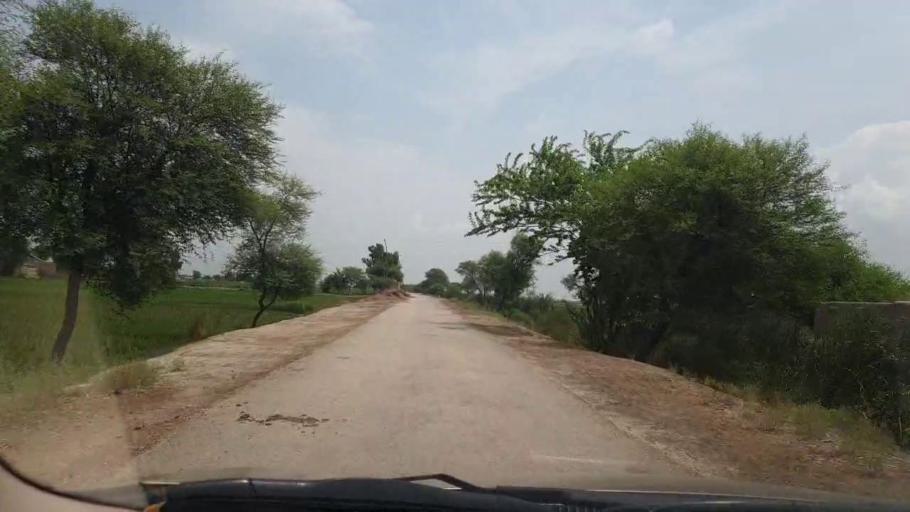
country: PK
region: Sindh
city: Larkana
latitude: 27.6078
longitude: 68.1572
